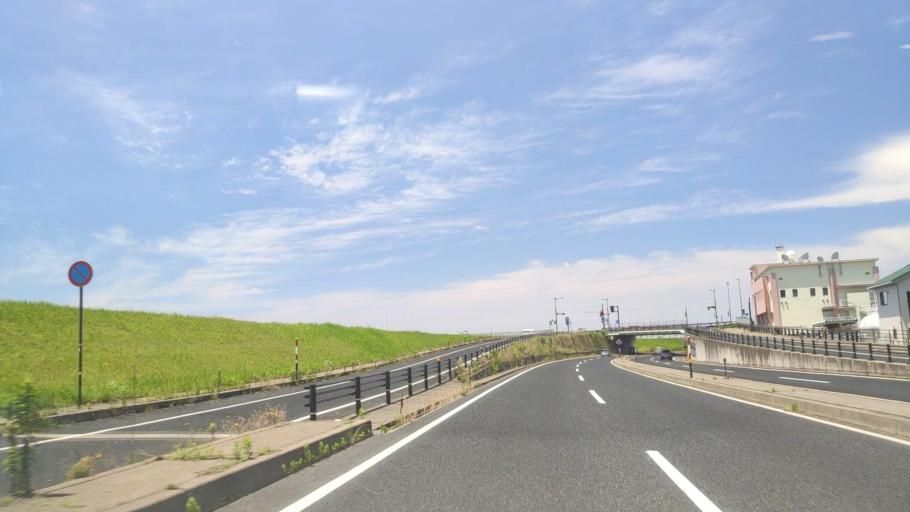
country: JP
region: Tottori
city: Tottori
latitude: 35.4946
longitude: 134.2181
